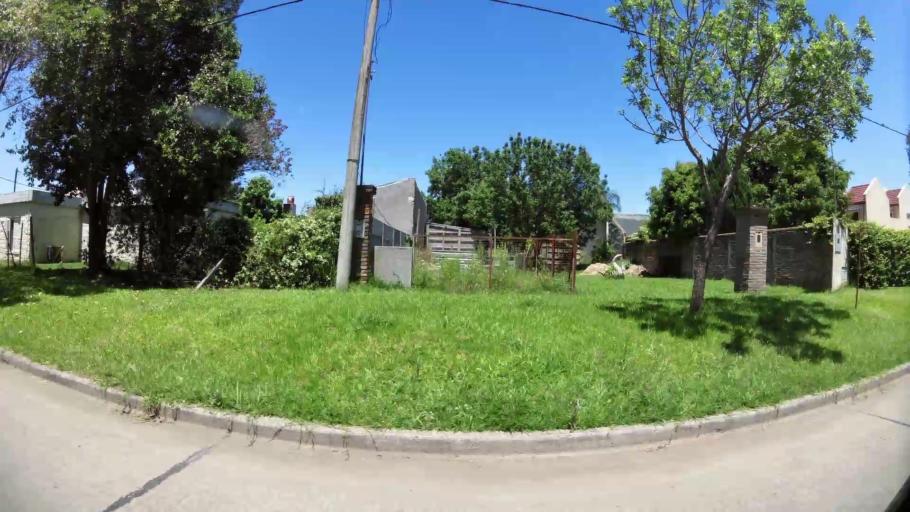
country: AR
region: Santa Fe
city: Rafaela
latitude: -31.2552
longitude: -61.4603
